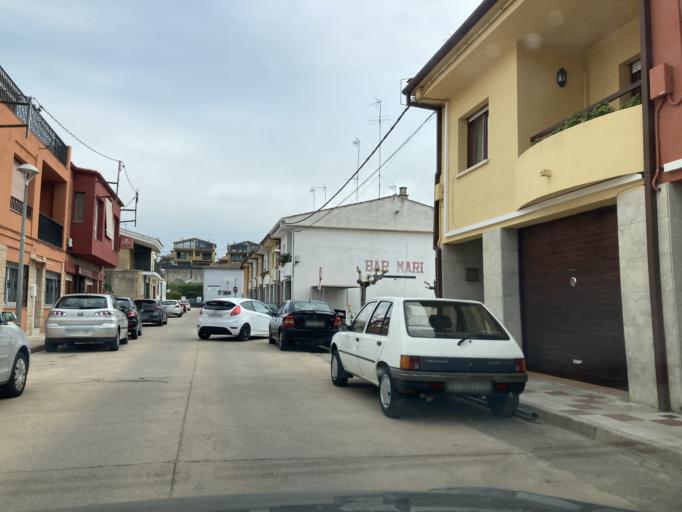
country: ES
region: Catalonia
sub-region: Provincia de Girona
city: Santa Coloma de Farners
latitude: 41.8659
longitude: 2.6586
